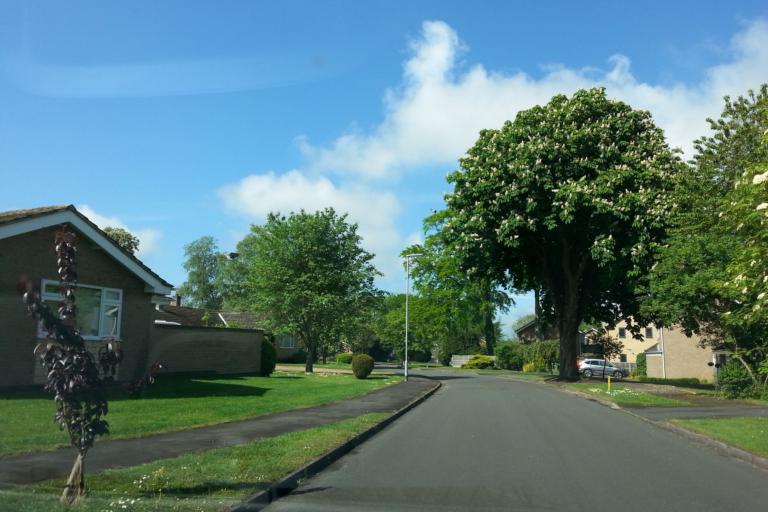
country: GB
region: England
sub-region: District of Rutland
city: Clipsham
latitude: 52.8081
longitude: -0.6157
